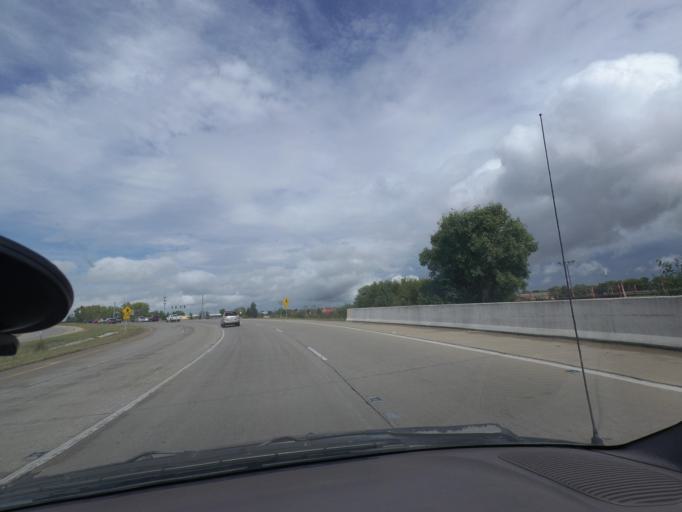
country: US
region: Indiana
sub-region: Marion County
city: Speedway
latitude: 39.8220
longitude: -86.2742
